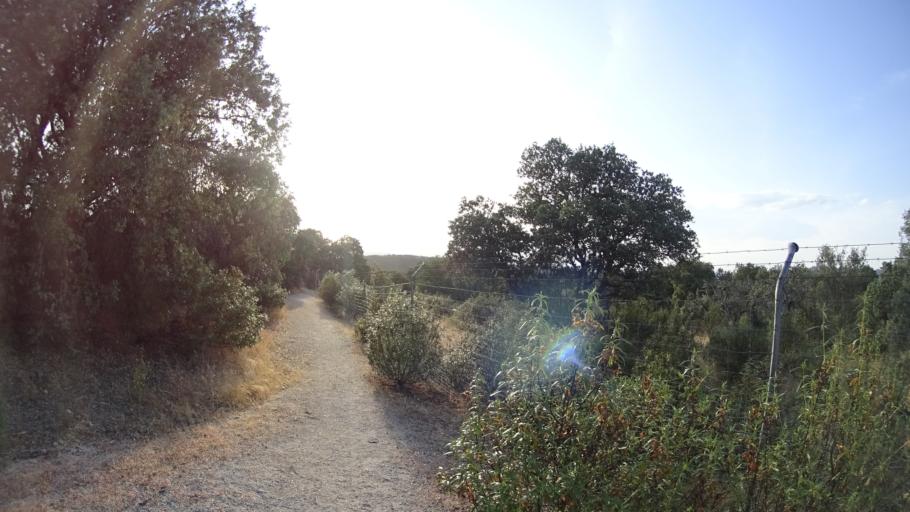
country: ES
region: Madrid
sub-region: Provincia de Madrid
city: Torrelodones
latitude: 40.5946
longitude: -3.9449
